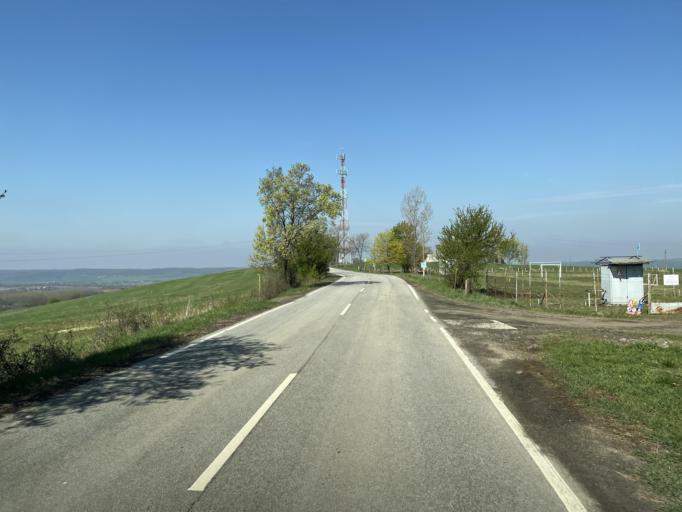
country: HU
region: Pest
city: Szob
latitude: 47.9366
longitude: 18.8164
